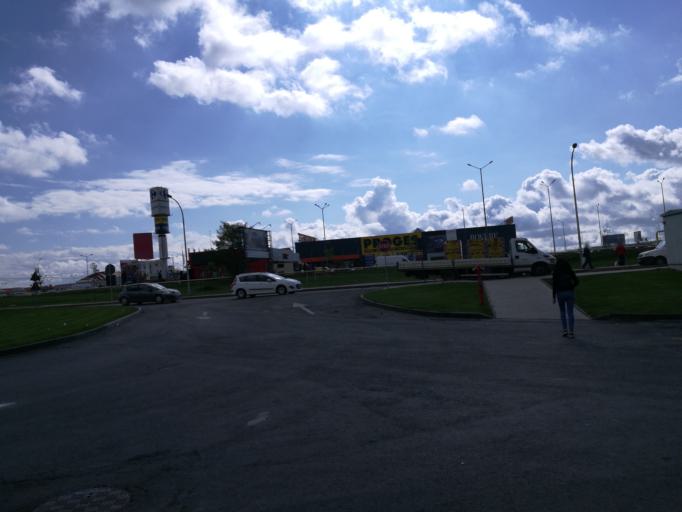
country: RO
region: Sibiu
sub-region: Municipiul Sibiu
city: Sibiu
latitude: 45.7793
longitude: 24.1681
